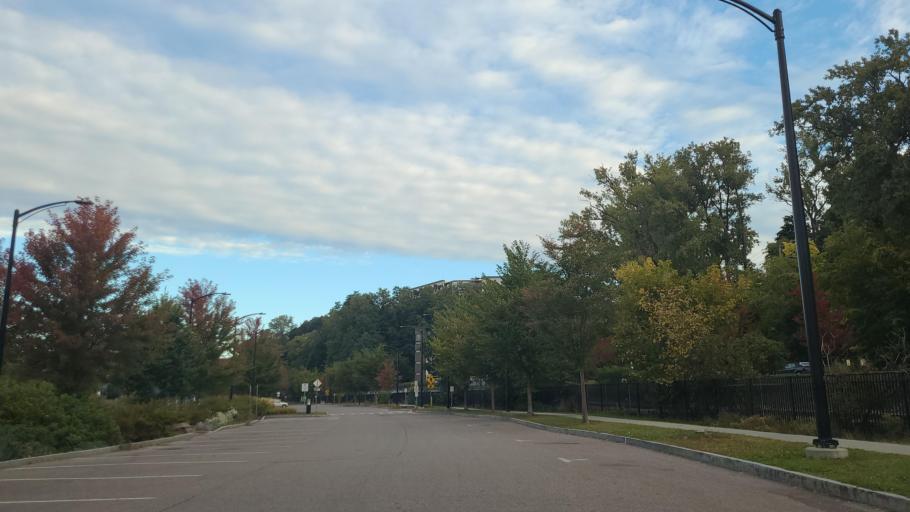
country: US
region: Vermont
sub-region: Chittenden County
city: Burlington
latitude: 44.4815
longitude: -73.2225
